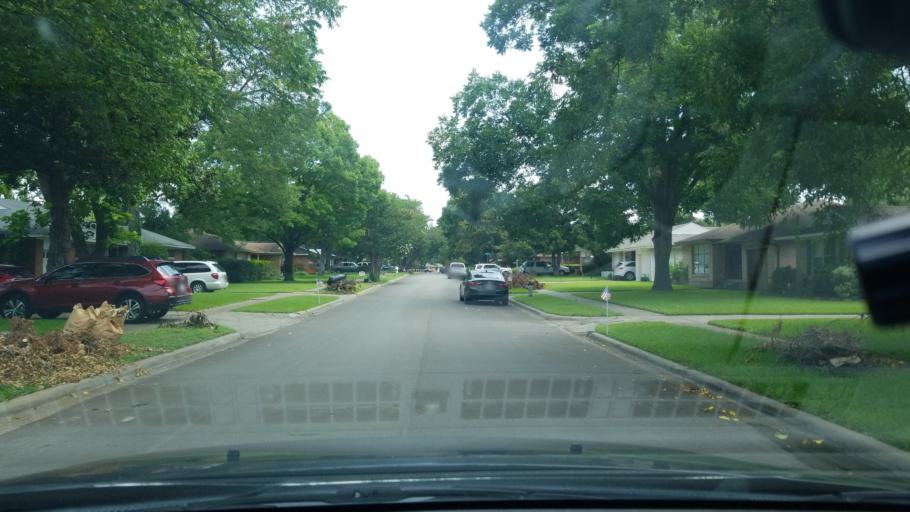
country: US
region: Texas
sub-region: Dallas County
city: Garland
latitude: 32.8300
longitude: -96.6857
